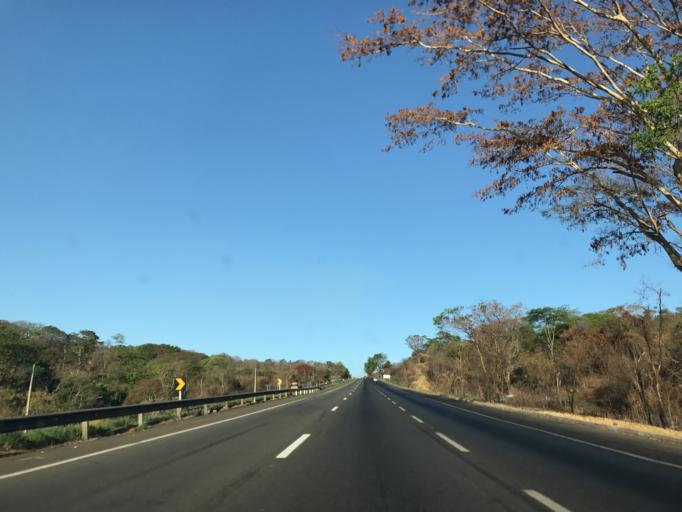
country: BR
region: Goias
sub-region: Goiania
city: Goiania
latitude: -16.5816
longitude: -49.1840
